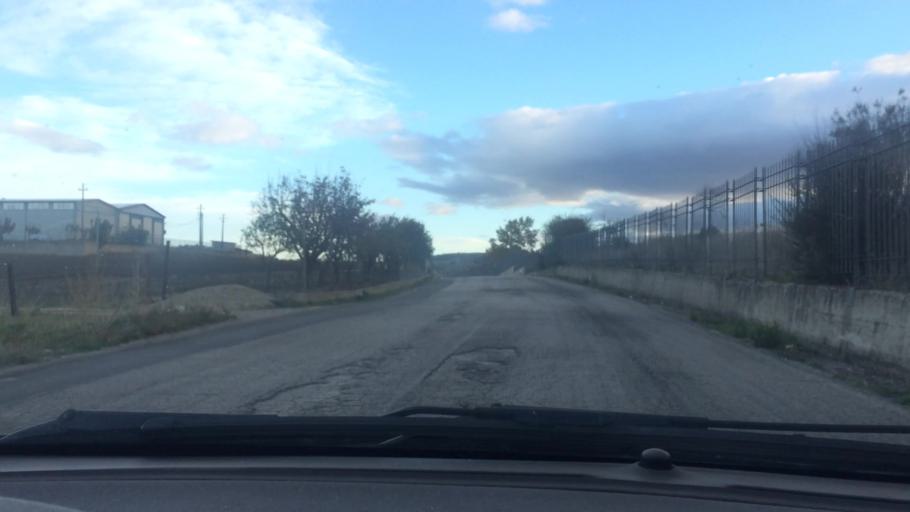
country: IT
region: Basilicate
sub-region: Provincia di Potenza
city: Tolve
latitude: 40.7099
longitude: 16.0188
